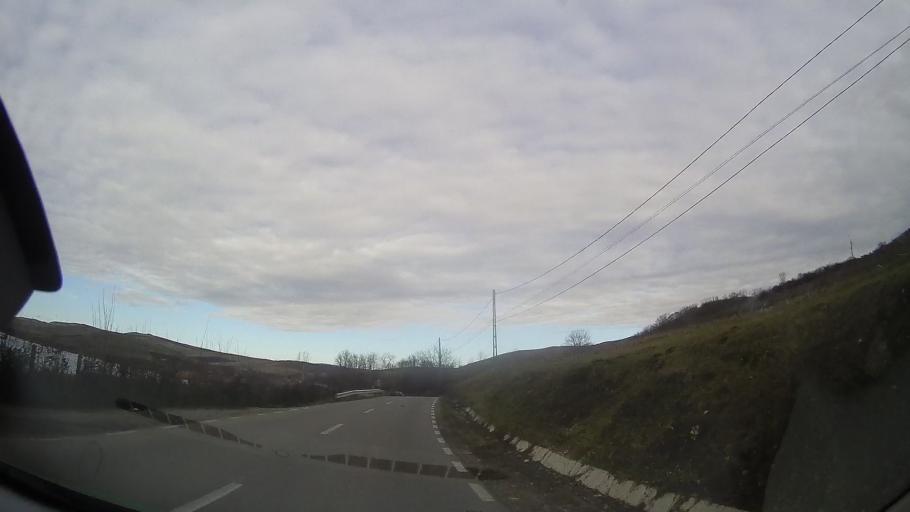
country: RO
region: Cluj
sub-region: Comuna Geaca
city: Geaca
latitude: 46.8369
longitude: 24.1341
